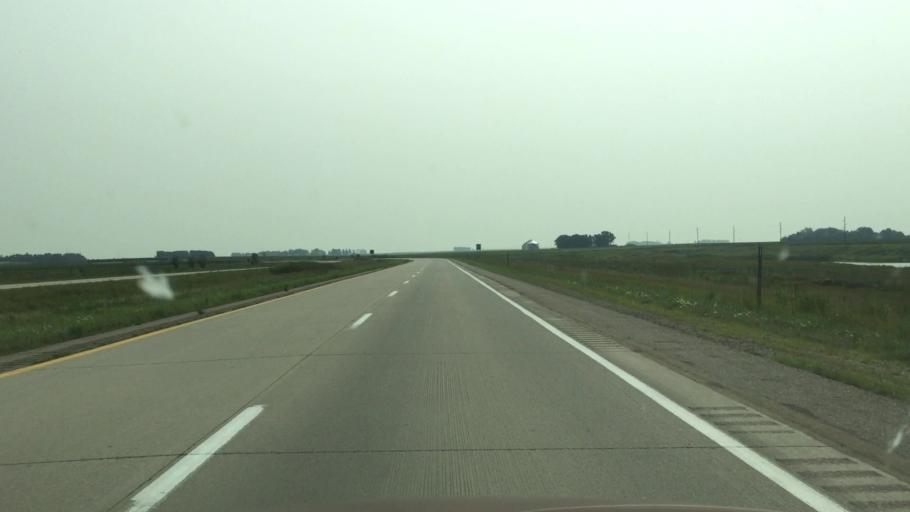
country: US
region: Iowa
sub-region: Osceola County
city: Sibley
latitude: 43.3843
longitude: -95.7357
